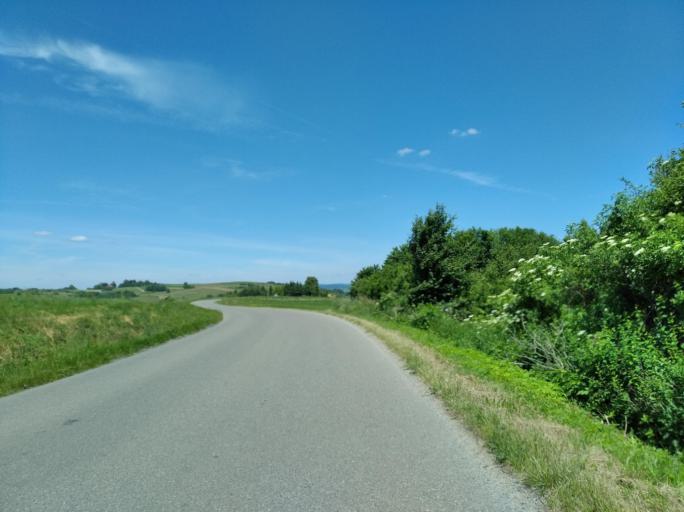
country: PL
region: Subcarpathian Voivodeship
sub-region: Powiat jasielski
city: Osiek Jasielski
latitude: 49.6753
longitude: 21.5422
